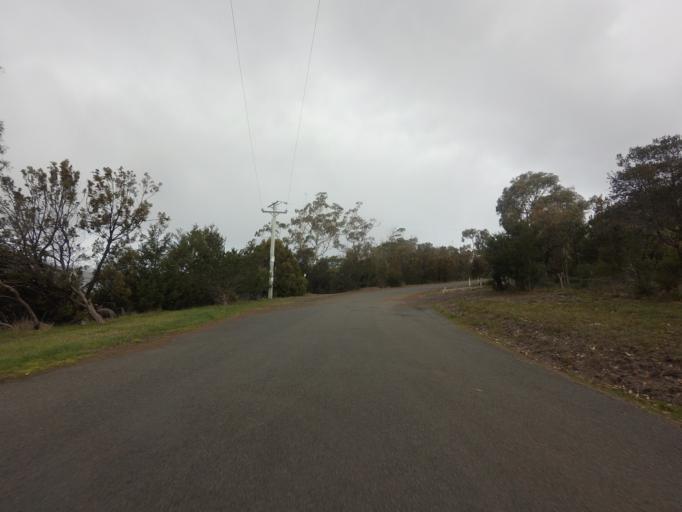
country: AU
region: Tasmania
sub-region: Sorell
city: Sorell
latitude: -42.5321
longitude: 147.9127
